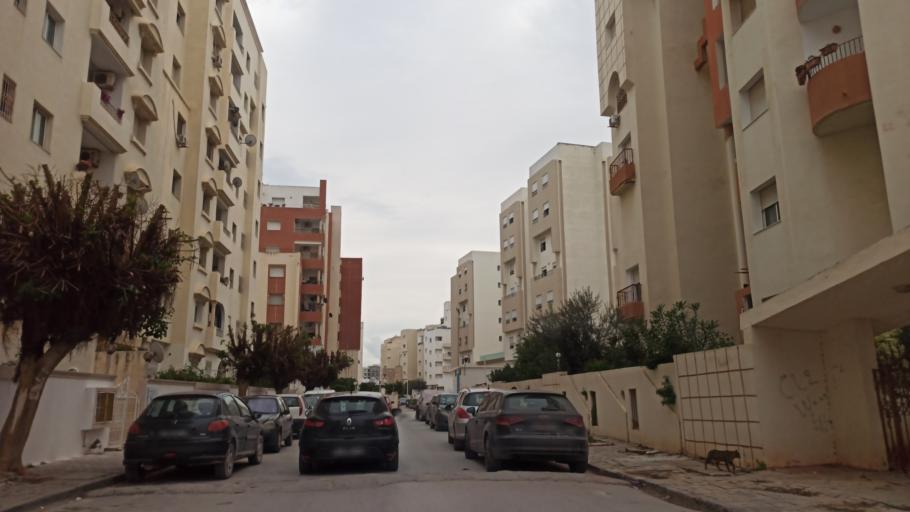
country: TN
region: Tunis
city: La Goulette
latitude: 36.8614
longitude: 10.2642
